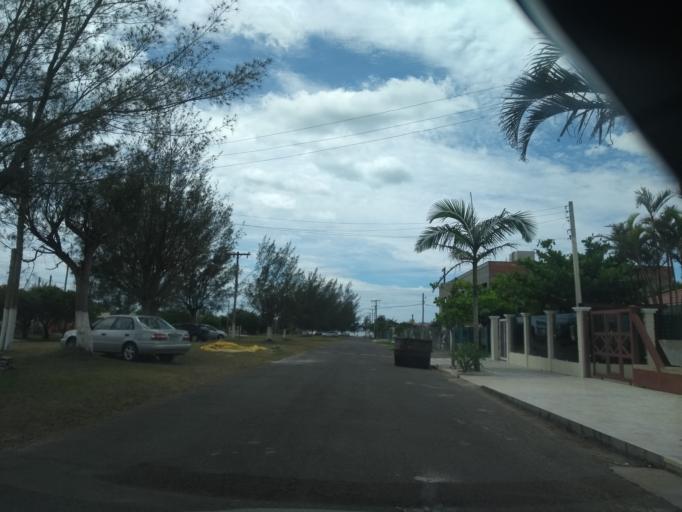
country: BR
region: Rio Grande do Sul
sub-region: Tramandai
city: Tramandai
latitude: -30.0624
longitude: -50.1627
